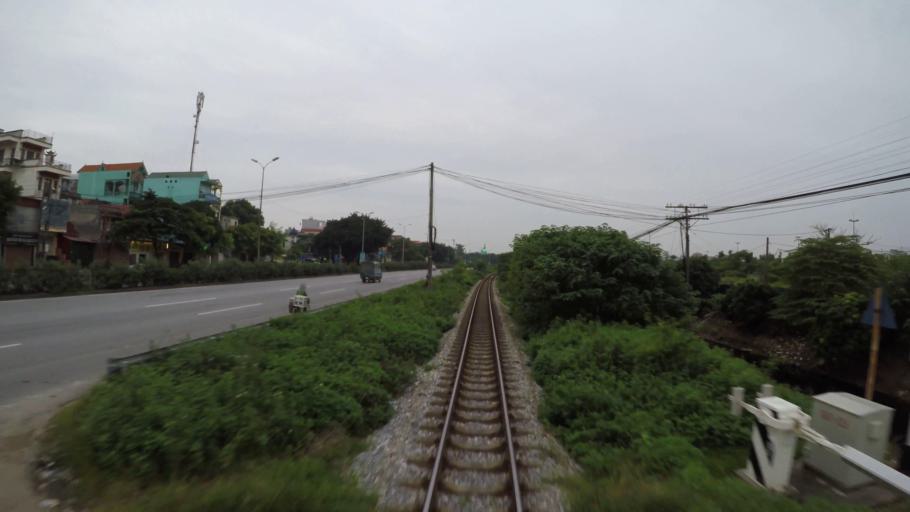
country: VN
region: Ha Noi
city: Trau Quy
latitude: 21.0113
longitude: 105.9516
